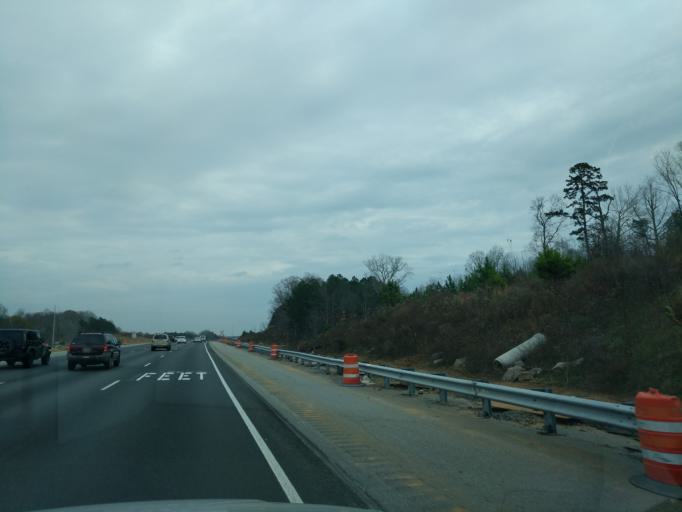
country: US
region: Georgia
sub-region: Gwinnett County
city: Sugar Hill
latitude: 34.0531
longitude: -84.0122
